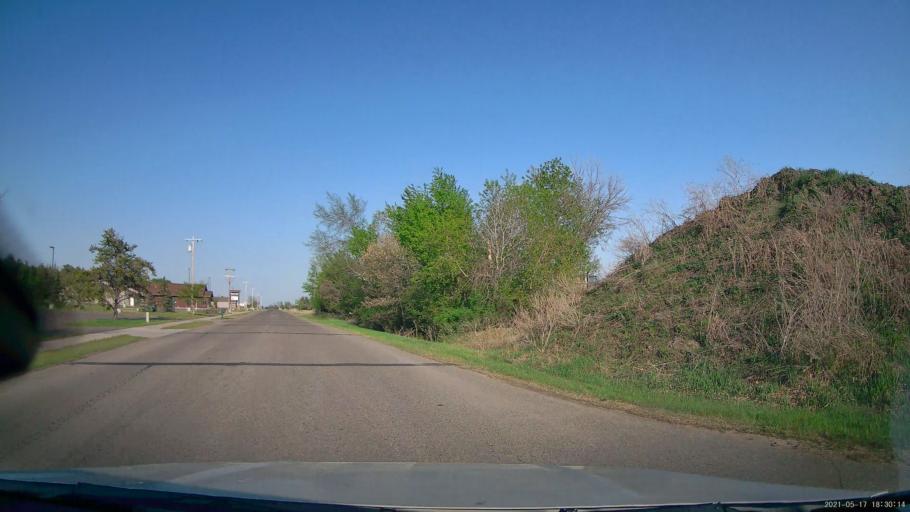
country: US
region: Minnesota
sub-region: Hubbard County
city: Park Rapids
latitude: 46.9249
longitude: -95.0416
